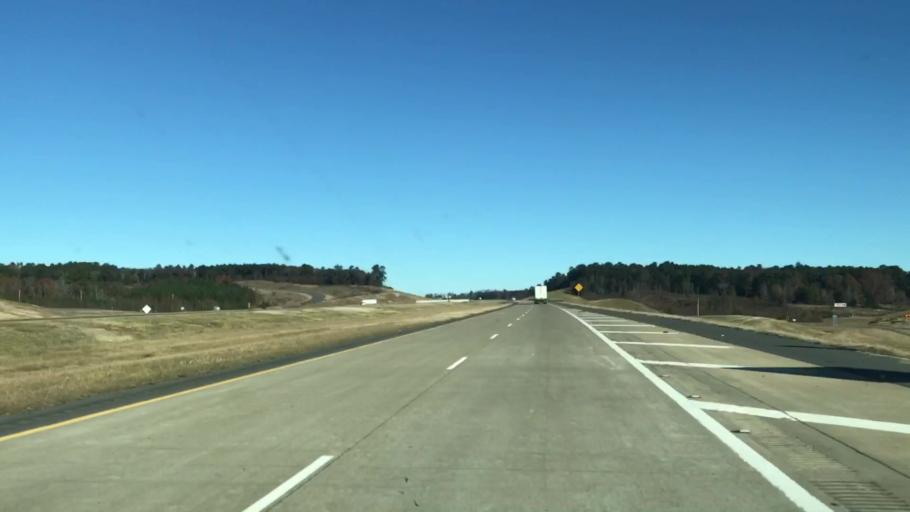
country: US
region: Louisiana
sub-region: Caddo Parish
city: Vivian
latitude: 32.9396
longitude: -93.8971
